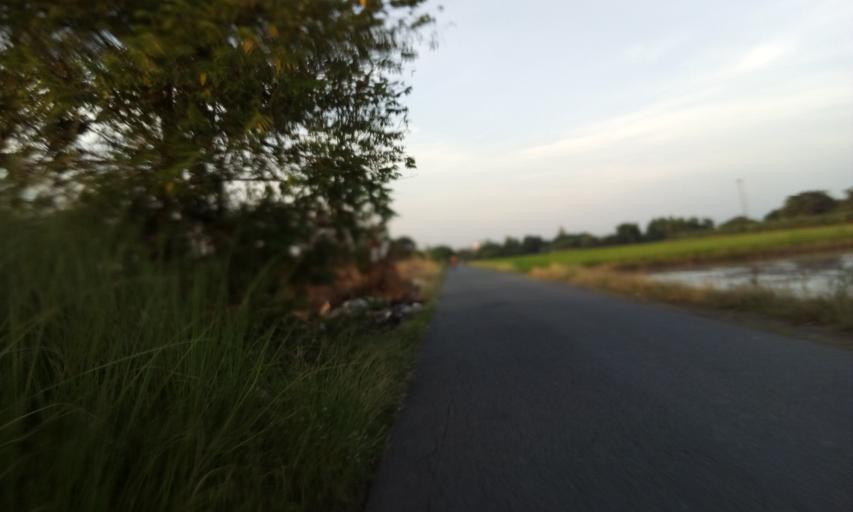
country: TH
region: Pathum Thani
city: Nong Suea
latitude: 14.0630
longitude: 100.8677
